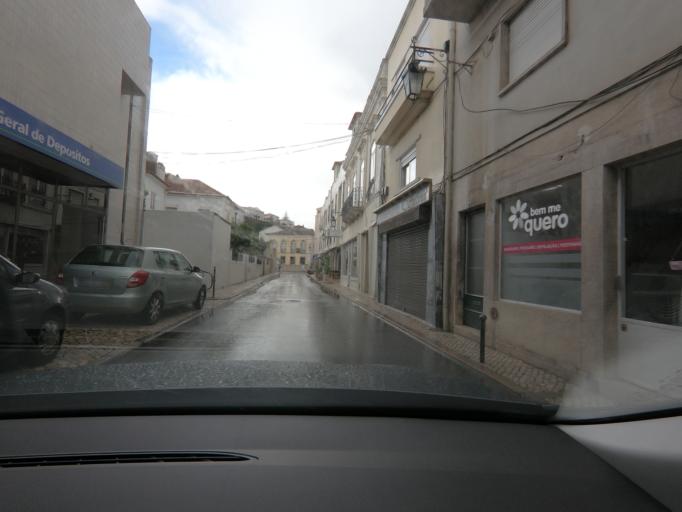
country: PT
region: Lisbon
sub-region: Alenquer
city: Alenquer
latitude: 39.0532
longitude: -9.0083
